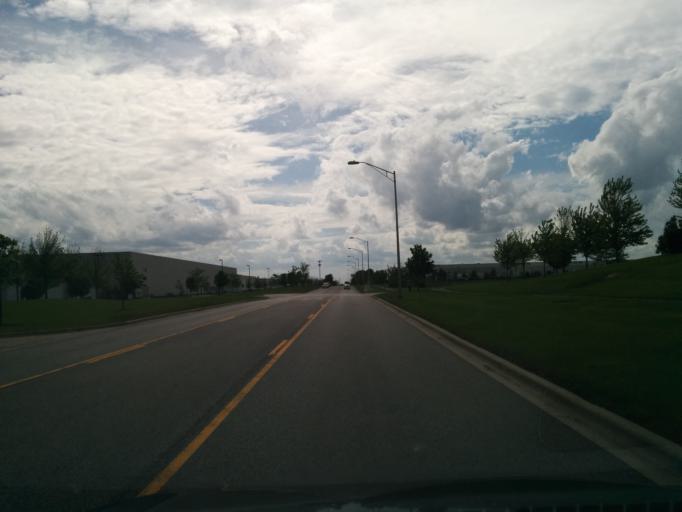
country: US
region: Illinois
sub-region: Will County
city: Romeoville
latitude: 41.6245
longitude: -88.1101
